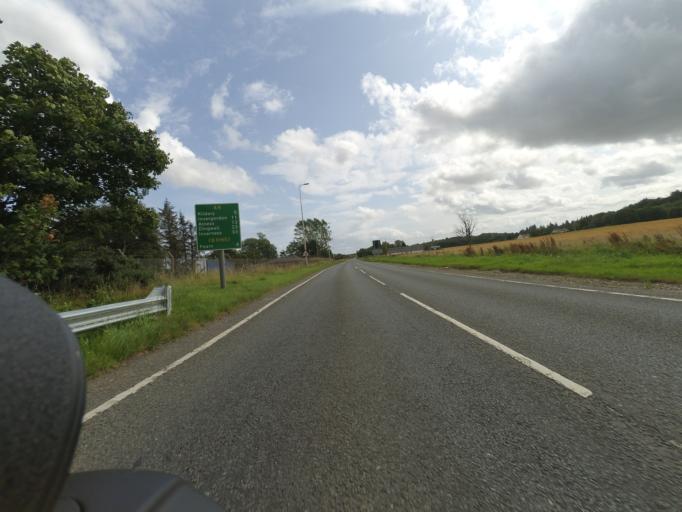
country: GB
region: Scotland
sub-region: Highland
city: Tain
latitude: 57.8005
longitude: -4.0419
